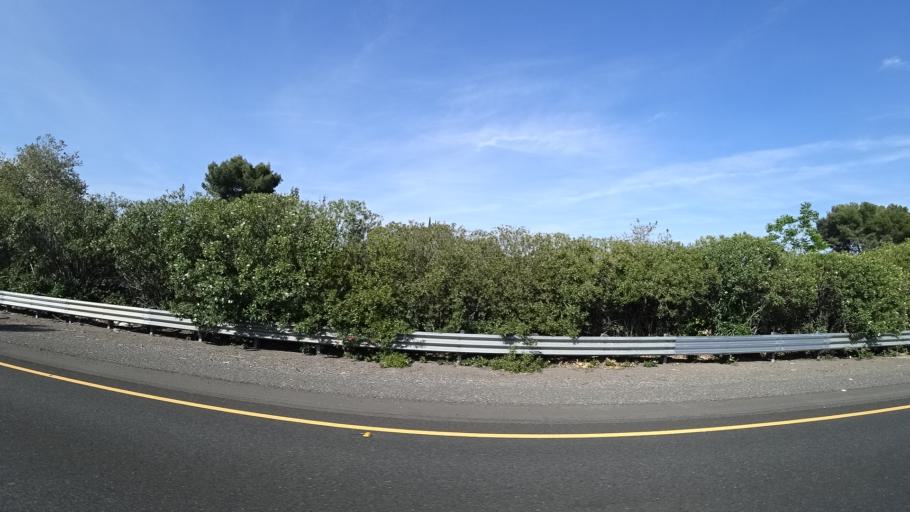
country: US
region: California
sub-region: Butte County
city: Chico
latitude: 39.7596
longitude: -121.8550
